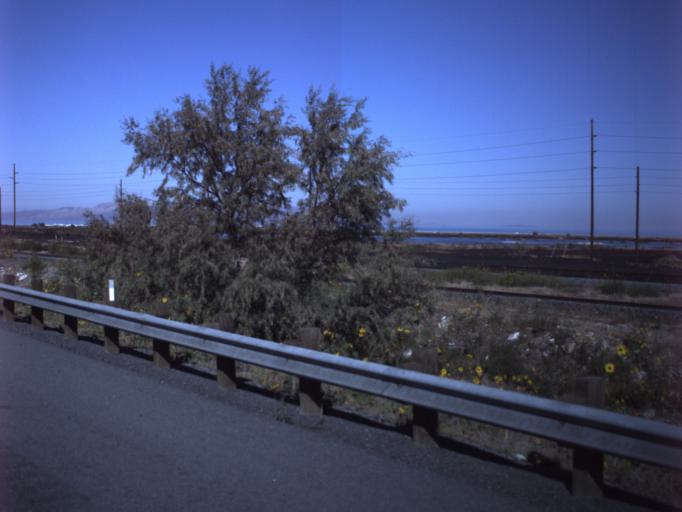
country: US
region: Utah
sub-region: Salt Lake County
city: Magna
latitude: 40.7274
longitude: -112.1917
